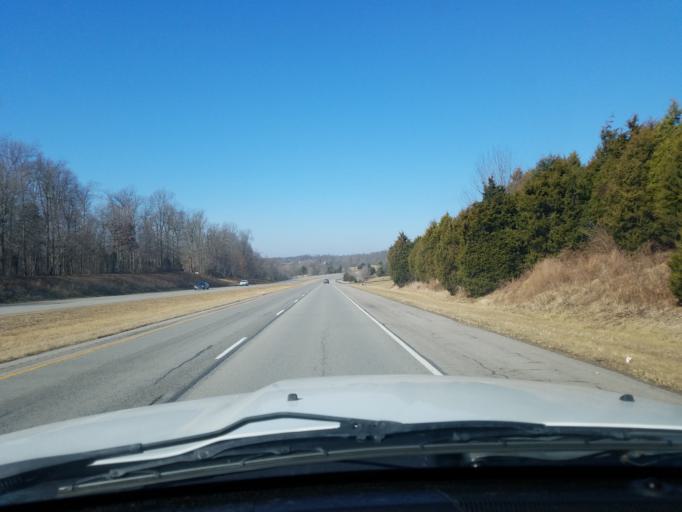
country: US
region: Kentucky
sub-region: Hardin County
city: Elizabethtown
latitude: 37.6376
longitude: -85.8329
